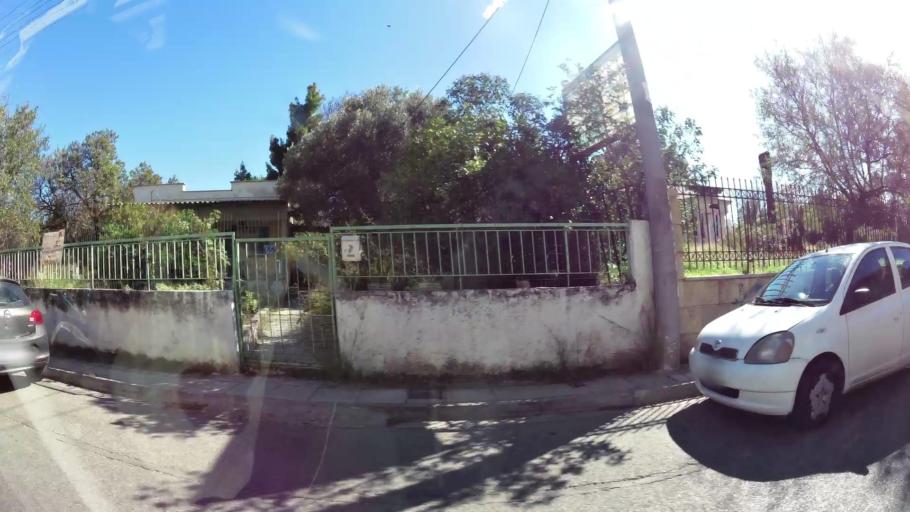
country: GR
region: Attica
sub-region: Nomarchia Athinas
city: Khalandrion
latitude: 38.0341
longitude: 23.8053
